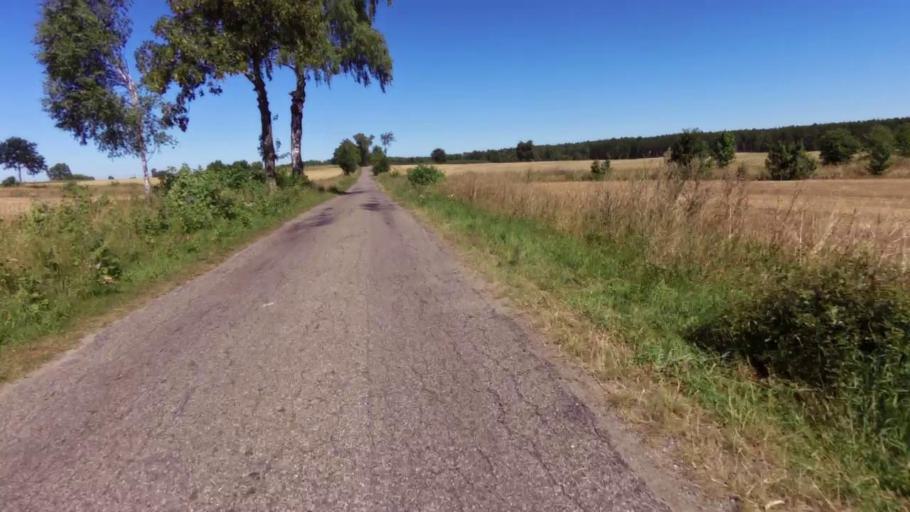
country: PL
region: West Pomeranian Voivodeship
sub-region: Powiat szczecinecki
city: Lubowo
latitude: 53.5653
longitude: 16.3574
